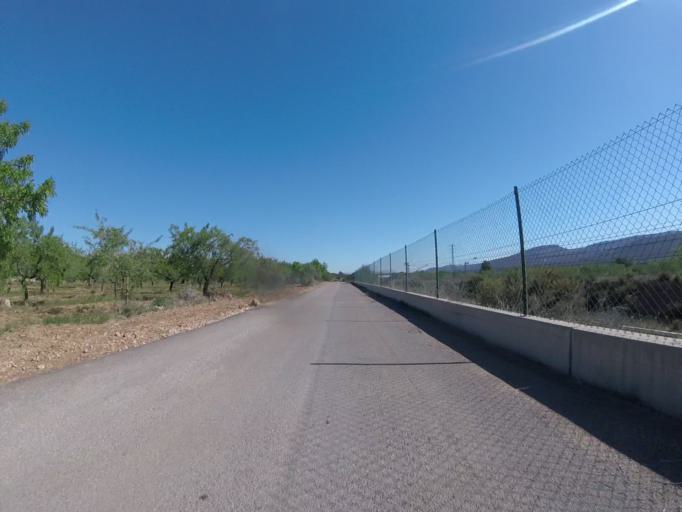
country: ES
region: Valencia
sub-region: Provincia de Castello
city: Alcala de Xivert
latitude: 40.3335
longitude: 0.2517
